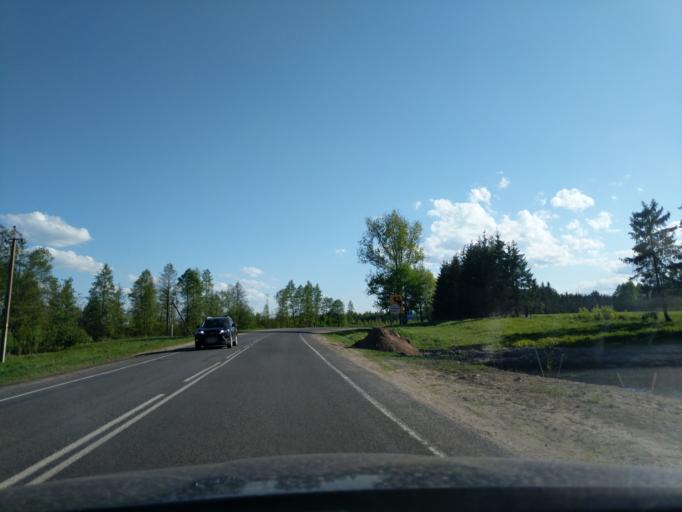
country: BY
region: Minsk
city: Myadzyel
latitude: 54.8618
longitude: 26.9325
